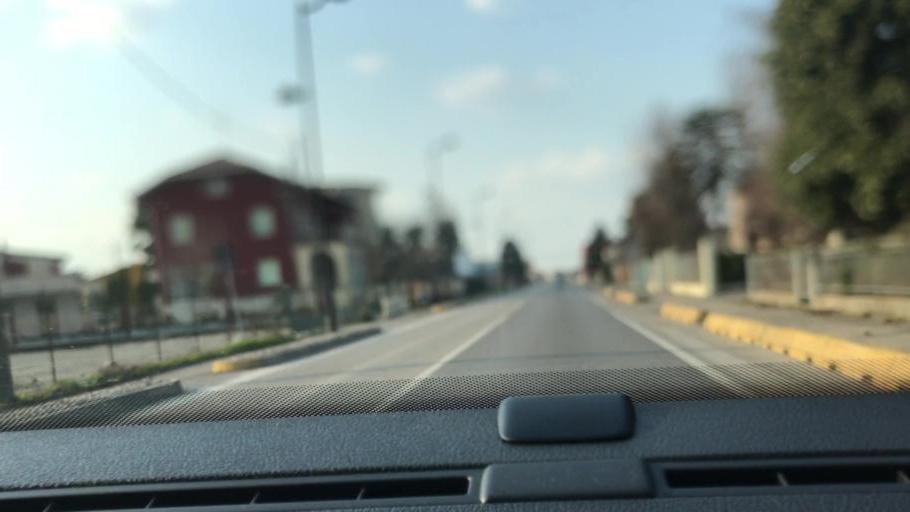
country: IT
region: Emilia-Romagna
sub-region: Provincia di Parma
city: Mezzano Inferiore
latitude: 44.9443
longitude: 10.4774
